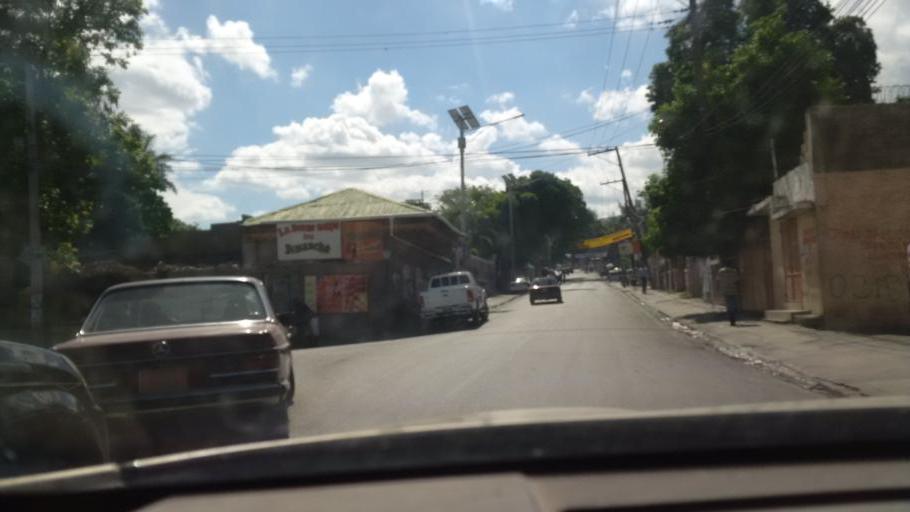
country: HT
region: Ouest
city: Port-au-Prince
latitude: 18.5350
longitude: -72.3297
